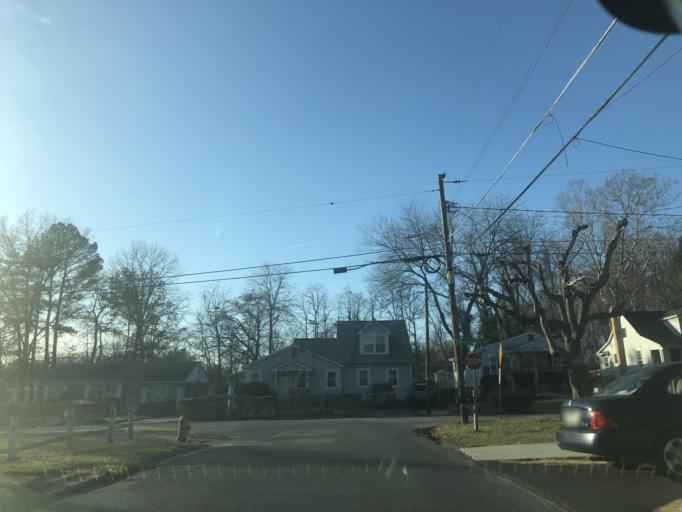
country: US
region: Maryland
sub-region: Baltimore County
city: Catonsville
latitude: 39.2821
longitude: -76.7368
